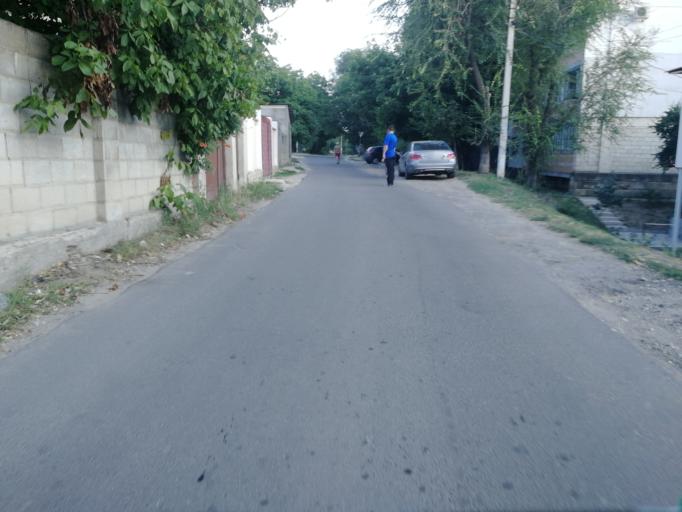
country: MD
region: Chisinau
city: Chisinau
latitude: 47.0267
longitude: 28.8745
